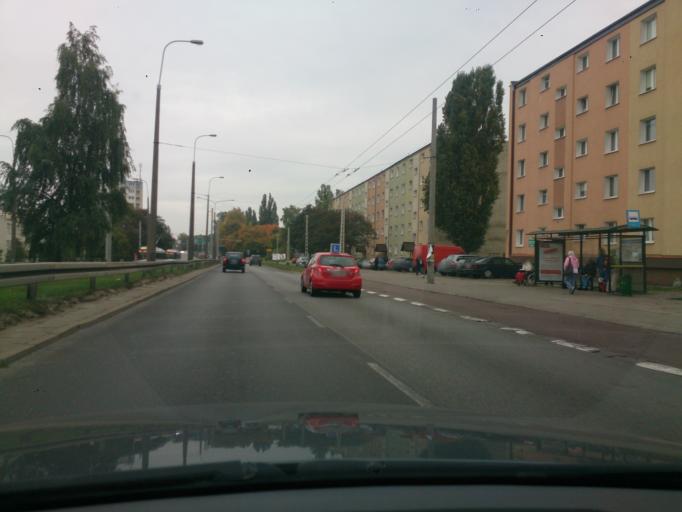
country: PL
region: Pomeranian Voivodeship
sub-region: Gdynia
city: Pogorze
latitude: 54.5354
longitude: 18.4801
